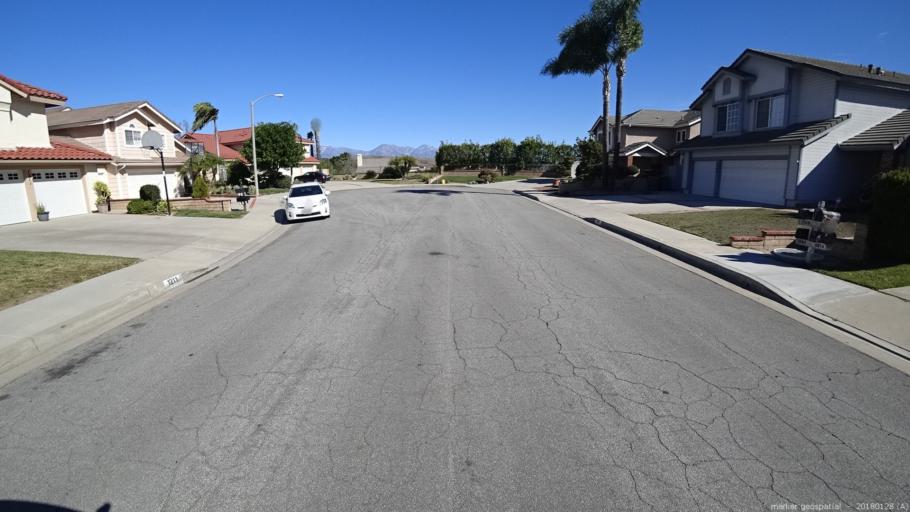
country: US
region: California
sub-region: San Bernardino County
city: Chino Hills
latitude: 33.9986
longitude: -117.7923
